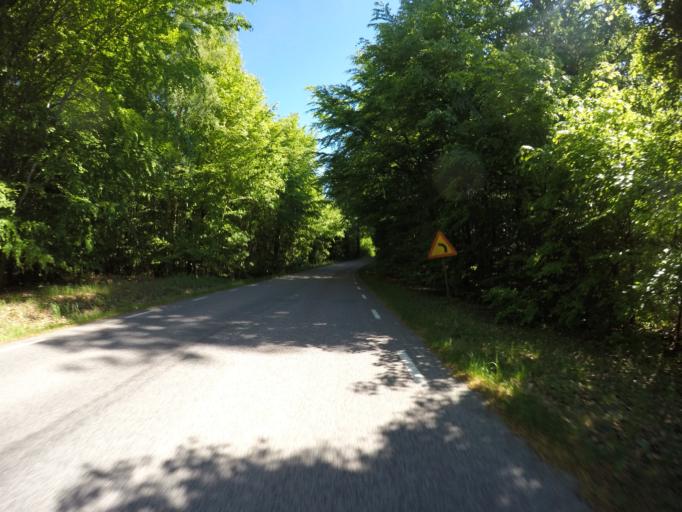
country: SE
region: Skane
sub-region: Svedala Kommun
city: Klagerup
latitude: 55.5567
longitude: 13.2121
